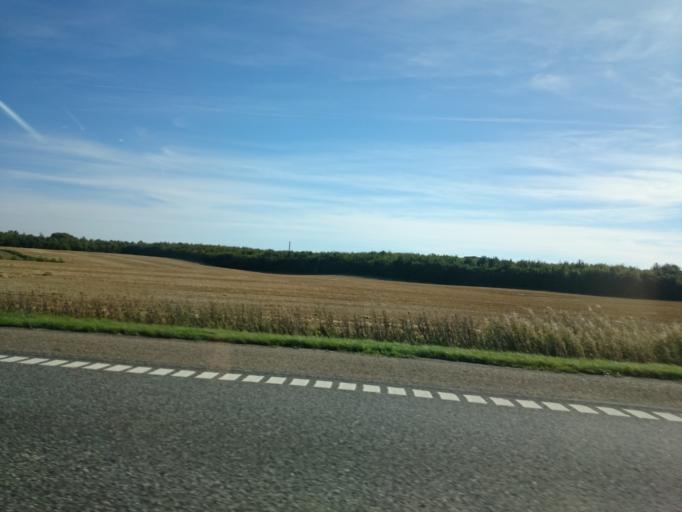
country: DK
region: Central Jutland
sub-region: Skanderborg Kommune
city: Horning
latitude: 56.0968
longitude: 10.0272
